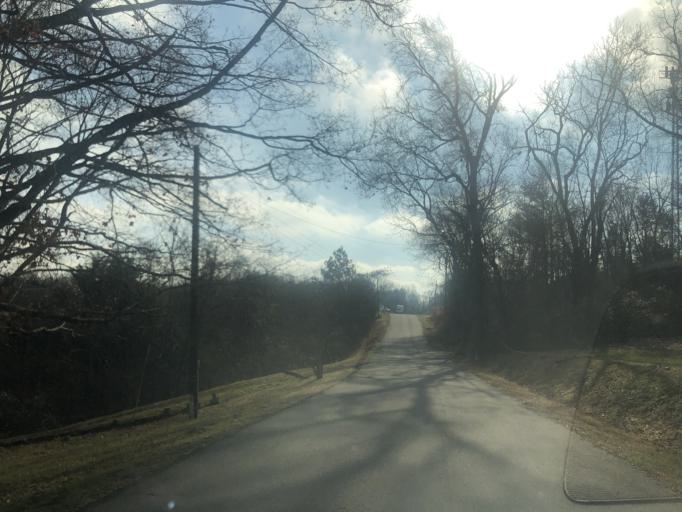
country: US
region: Tennessee
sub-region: Rutherford County
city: La Vergne
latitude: 36.0650
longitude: -86.6530
